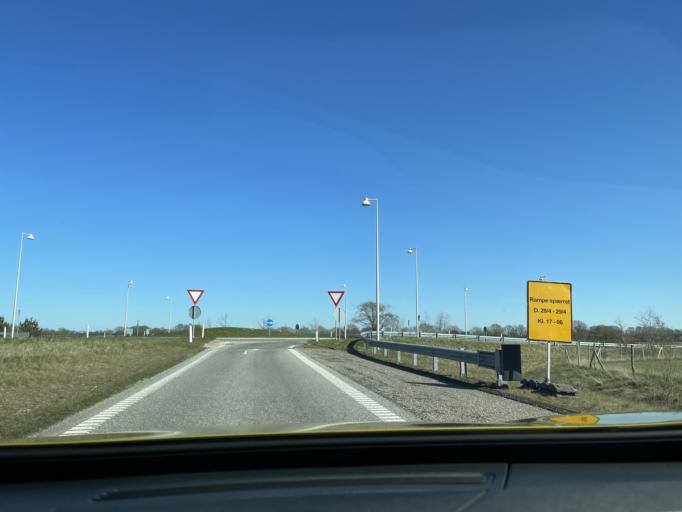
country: DK
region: Central Jutland
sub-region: Ikast-Brande Kommune
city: Bording Kirkeby
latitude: 56.1334
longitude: 9.2651
